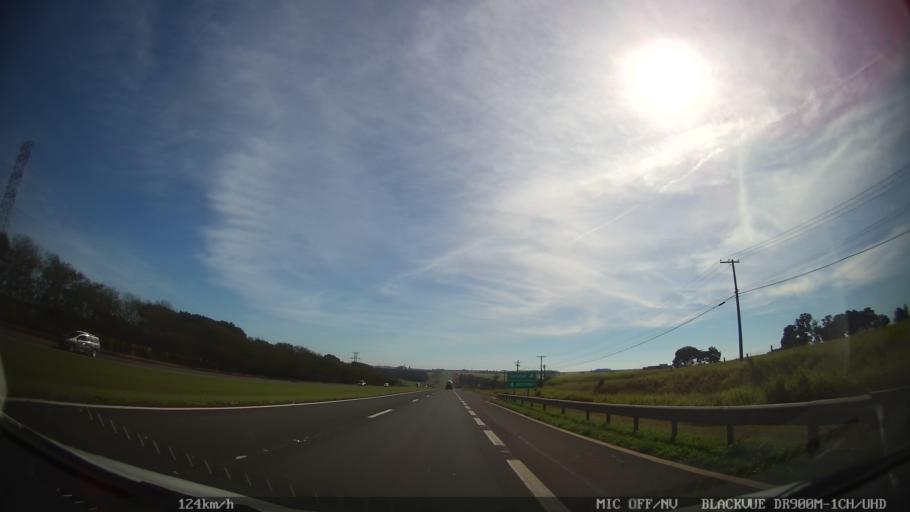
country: BR
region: Sao Paulo
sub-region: Araras
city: Araras
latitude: -22.3177
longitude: -47.3903
